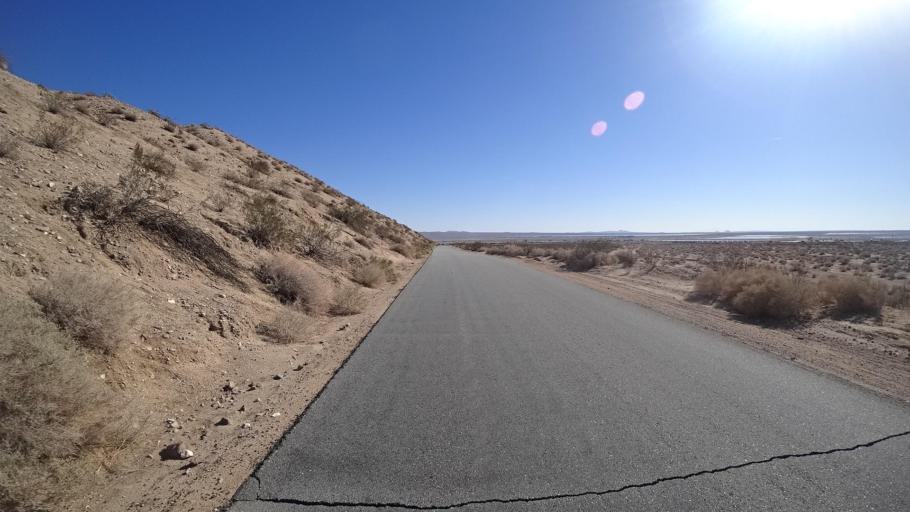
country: US
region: California
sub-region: Kern County
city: California City
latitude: 35.3034
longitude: -118.0067
